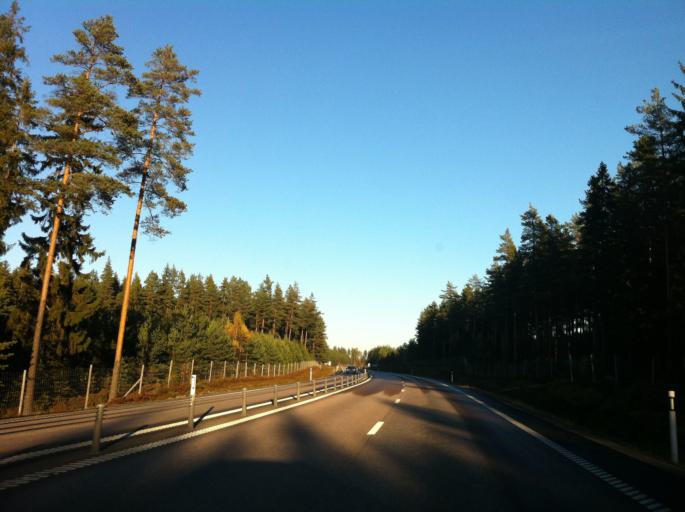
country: SE
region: Dalarna
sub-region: Hedemora Kommun
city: Langshyttan
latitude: 60.5657
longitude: 15.9519
